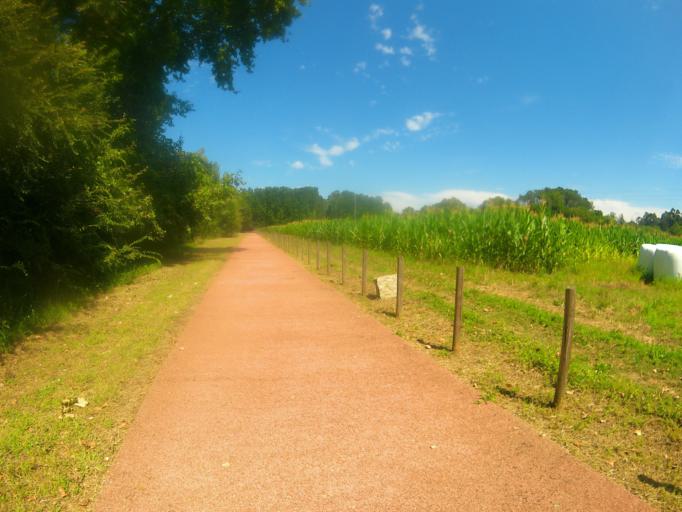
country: PT
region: Viana do Castelo
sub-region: Valenca
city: Valenca
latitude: 41.9899
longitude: -8.6778
